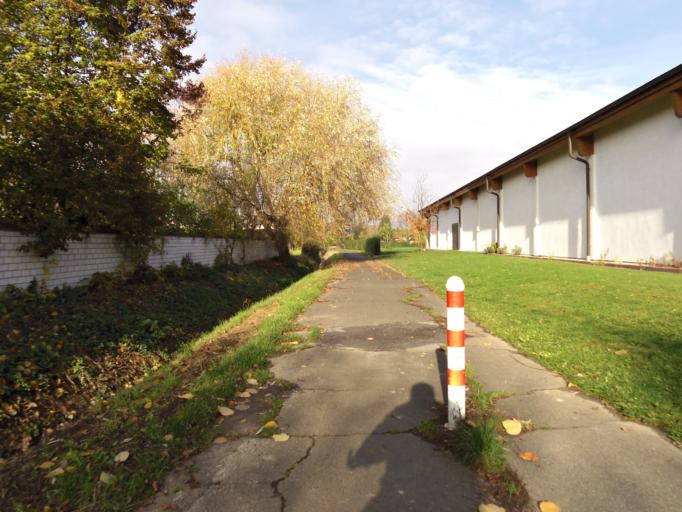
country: DE
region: Rheinland-Pfalz
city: Laumersheim
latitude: 49.5526
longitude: 8.2392
